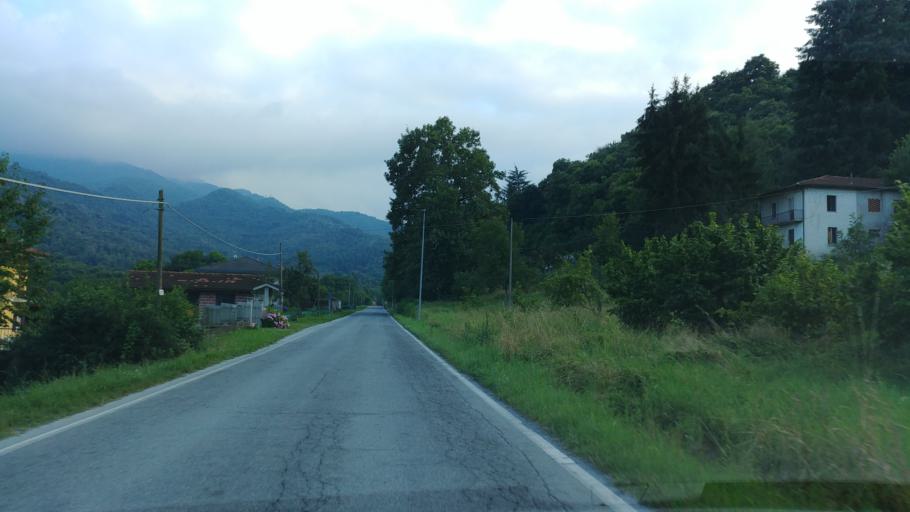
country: IT
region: Piedmont
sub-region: Provincia di Cuneo
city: Peveragno
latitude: 44.3260
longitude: 7.6017
